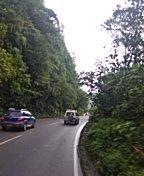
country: CR
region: San Jose
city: Dulce Nombre de Jesus
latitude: 10.0830
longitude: -83.9816
